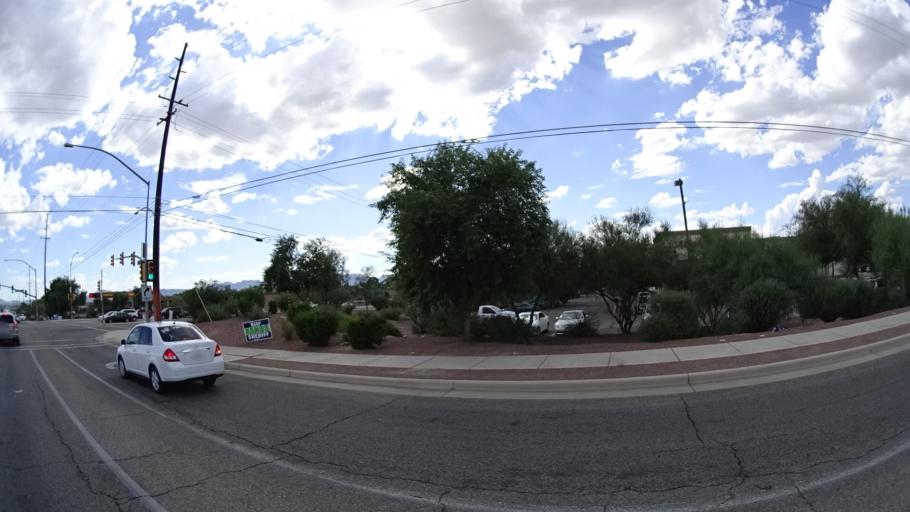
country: US
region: Arizona
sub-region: Pima County
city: Casas Adobes
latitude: 32.3237
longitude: -111.0123
